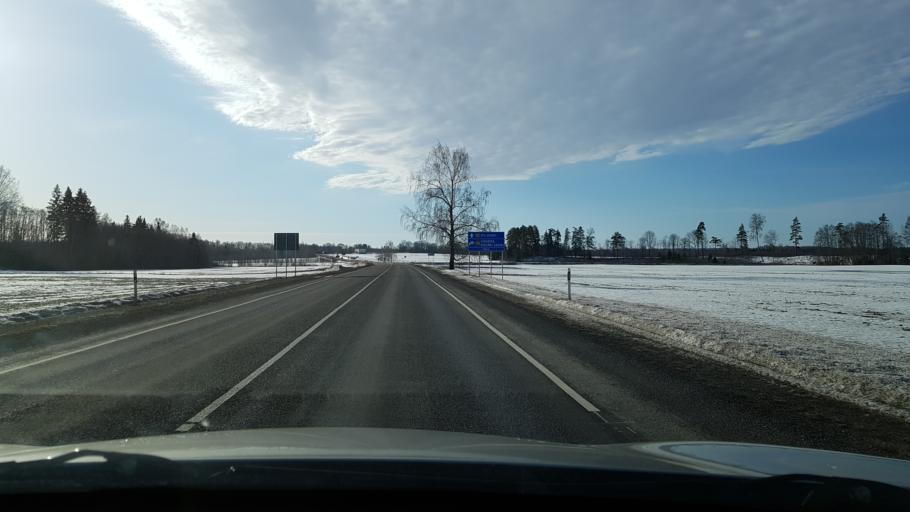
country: EE
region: Viljandimaa
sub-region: Vohma linn
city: Vohma
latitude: 58.5190
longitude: 25.5861
